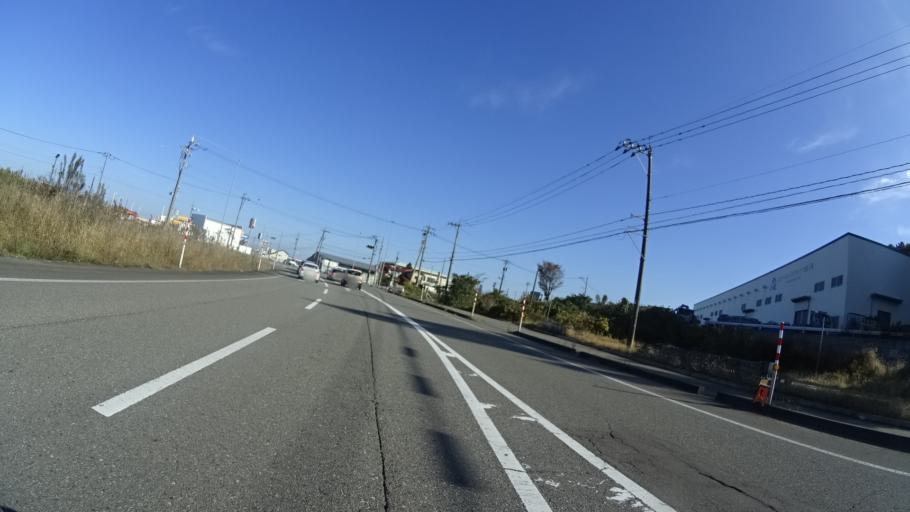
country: JP
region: Ishikawa
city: Komatsu
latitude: 36.3158
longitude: 136.3909
